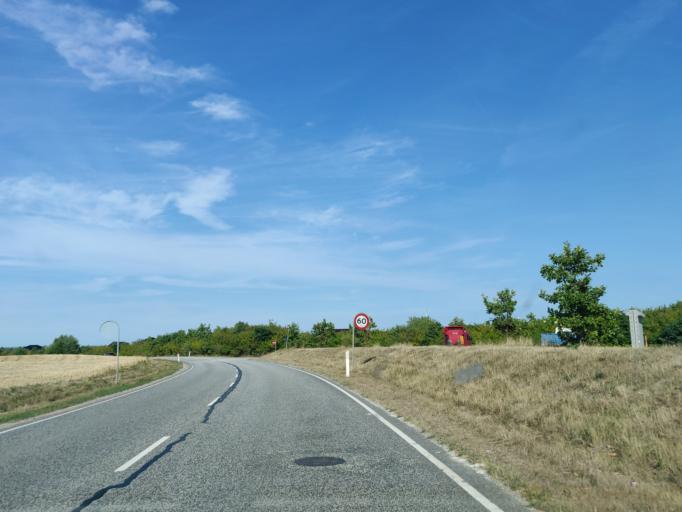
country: DK
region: Zealand
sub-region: Roskilde Kommune
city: Svogerslev
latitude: 55.6300
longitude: 12.0418
